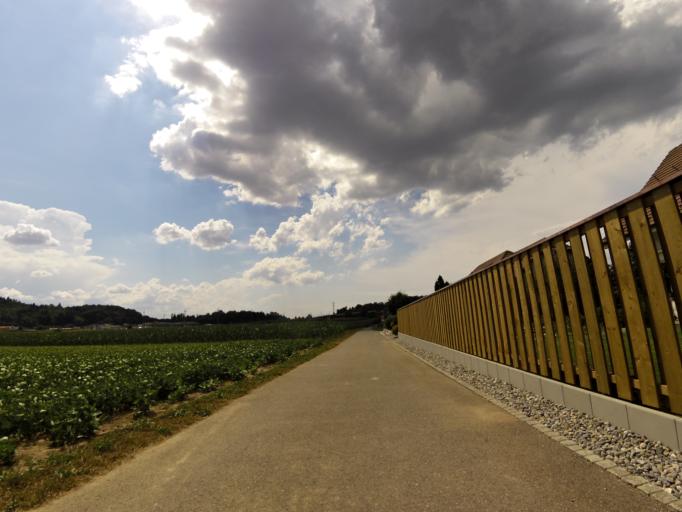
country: CH
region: Aargau
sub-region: Bezirk Lenzburg
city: Othmarsingen
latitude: 47.3973
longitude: 8.2130
